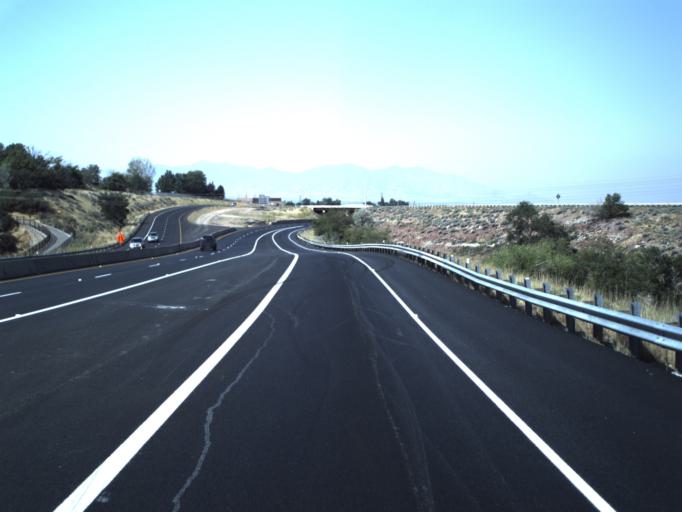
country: US
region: Utah
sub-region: Salt Lake County
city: Canyon Rim
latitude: 40.7137
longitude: -111.8131
